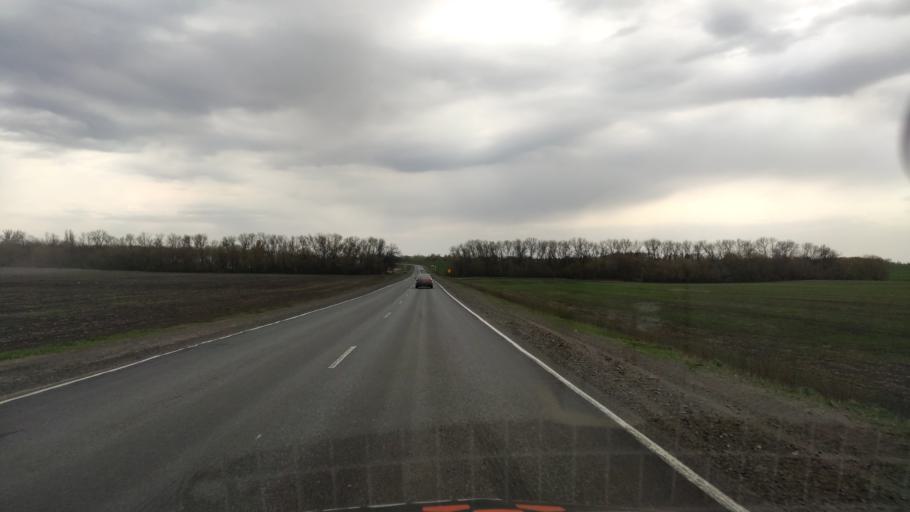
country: RU
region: Kursk
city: Gorshechnoye
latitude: 51.5425
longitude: 38.0254
